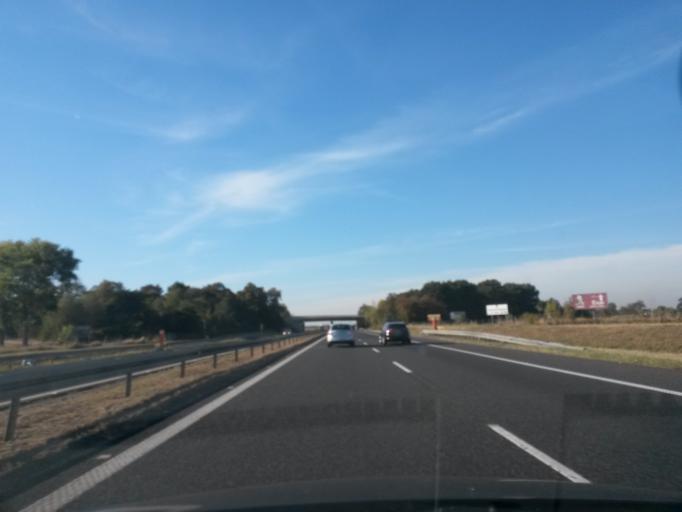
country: PL
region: Lower Silesian Voivodeship
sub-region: Powiat wroclawski
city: Zorawina
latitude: 50.9994
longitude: 17.0413
